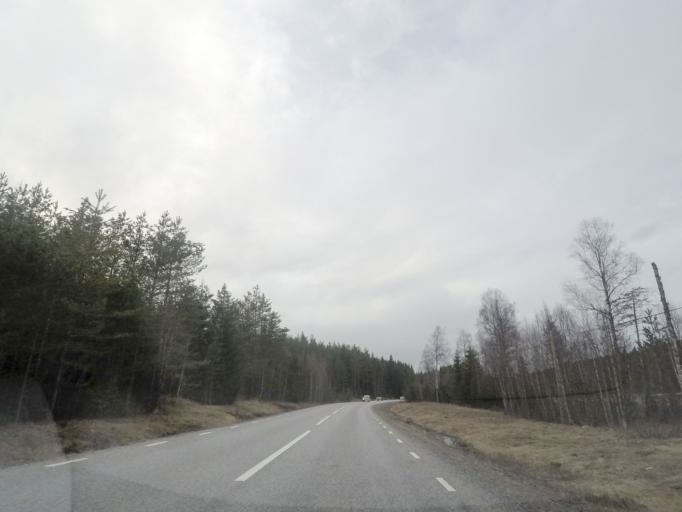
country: SE
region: OErebro
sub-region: Ljusnarsbergs Kommun
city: Kopparberg
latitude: 59.8968
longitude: 15.1005
